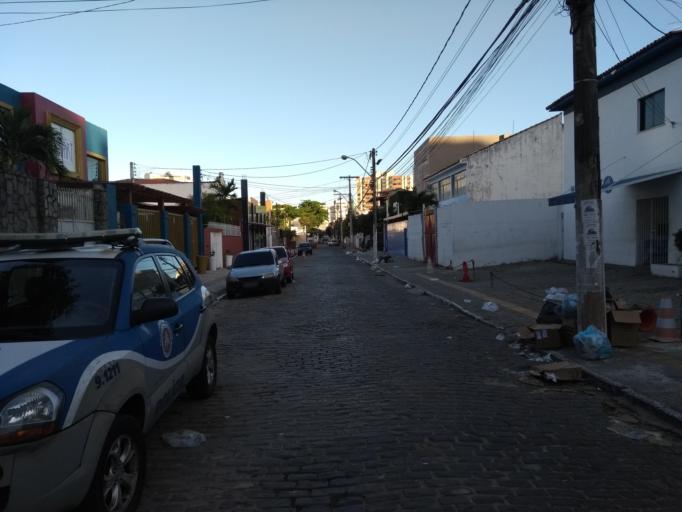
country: BR
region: Bahia
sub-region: Salvador
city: Salvador
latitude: -13.0096
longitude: -38.4914
